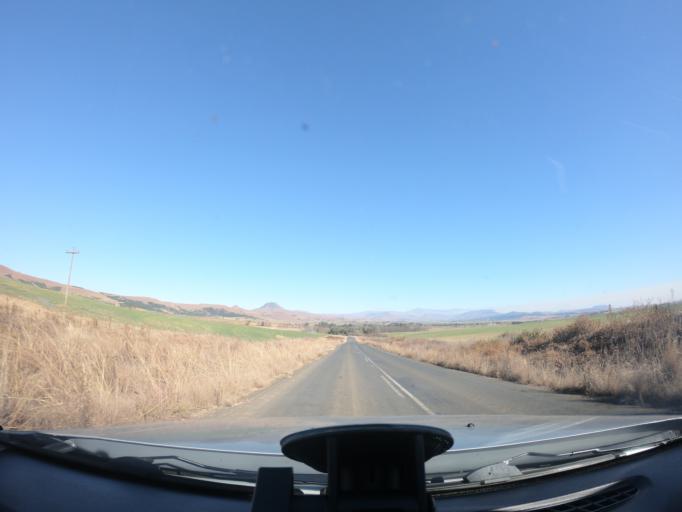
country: ZA
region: KwaZulu-Natal
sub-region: uMgungundlovu District Municipality
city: Mooirivier
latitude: -29.3262
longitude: 29.8544
